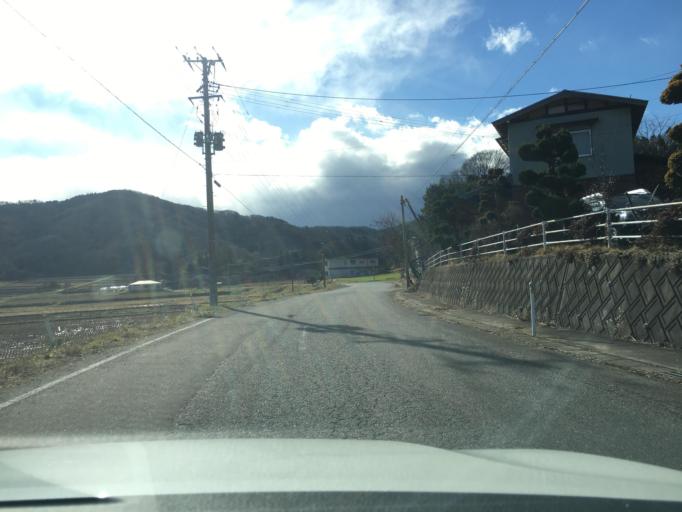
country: JP
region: Fukushima
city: Funehikimachi-funehiki
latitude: 37.3623
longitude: 140.6185
